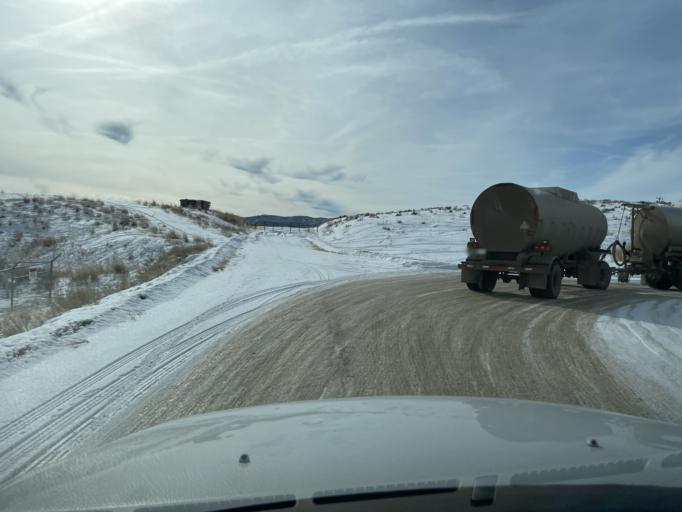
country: US
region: Colorado
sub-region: Moffat County
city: Craig
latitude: 40.3111
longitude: -107.6933
